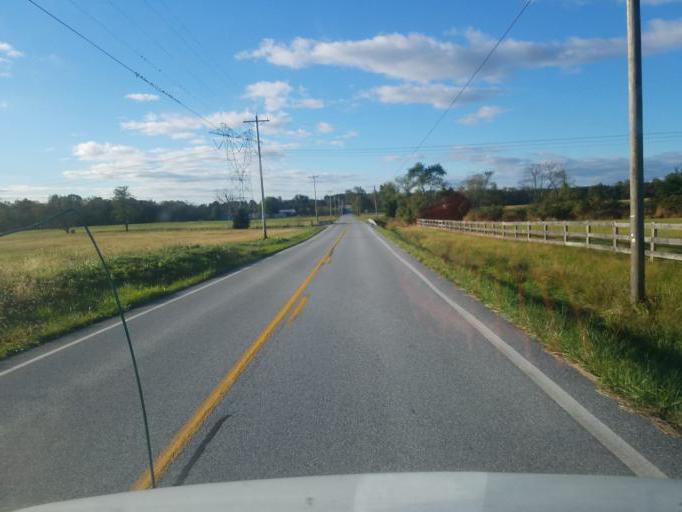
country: US
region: Pennsylvania
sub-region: Adams County
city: Gettysburg
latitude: 39.8808
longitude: -77.2298
